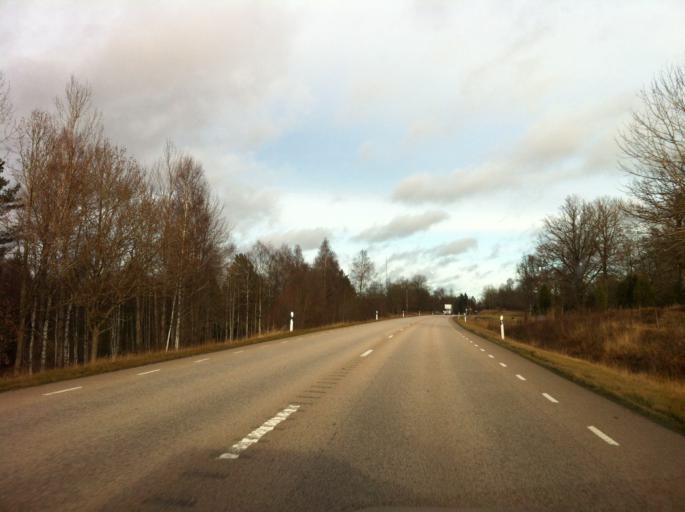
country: SE
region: Kronoberg
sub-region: Uppvidinge Kommun
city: Aseda
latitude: 57.1194
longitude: 15.2371
